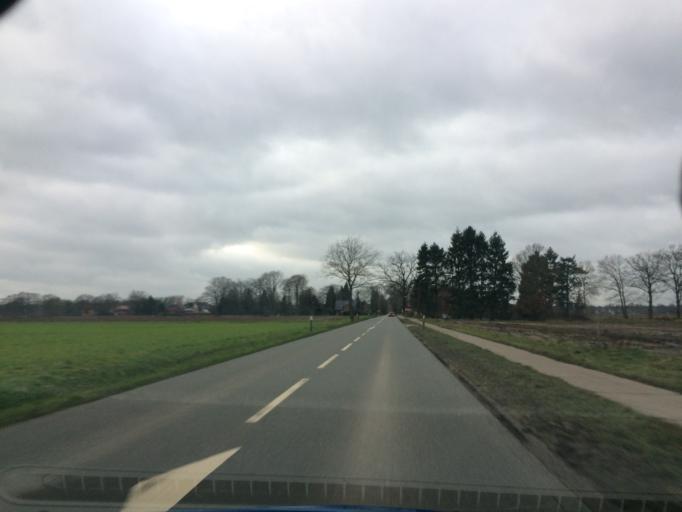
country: DE
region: Lower Saxony
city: Radbruch
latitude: 53.3065
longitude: 10.3056
